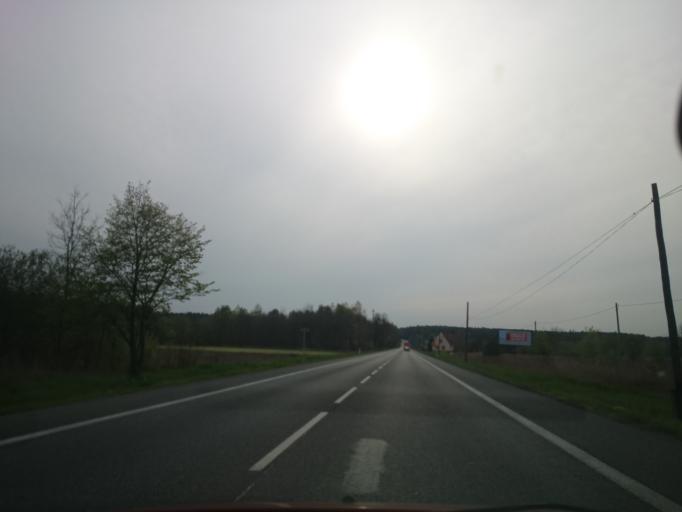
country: PL
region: Opole Voivodeship
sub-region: Powiat opolski
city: Dabrowa
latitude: 50.6887
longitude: 17.7510
